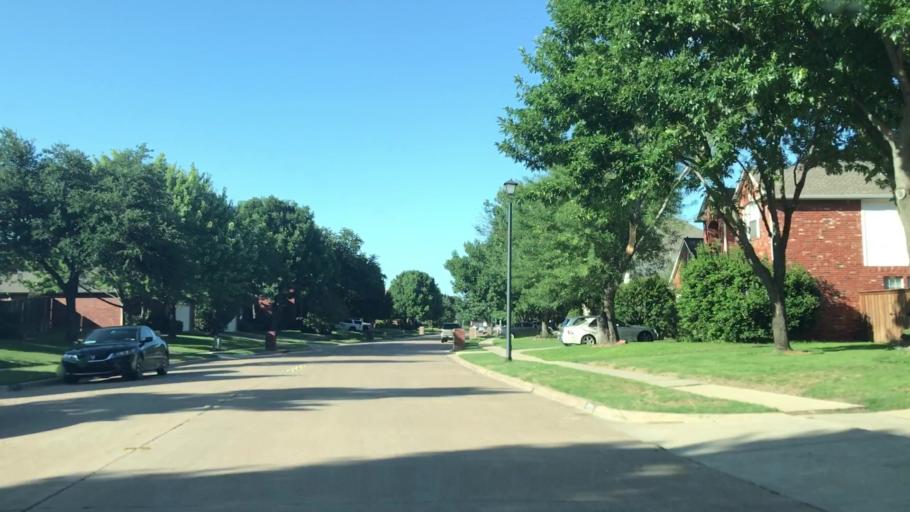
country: US
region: Texas
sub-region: Collin County
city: Frisco
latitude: 33.1192
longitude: -96.7806
